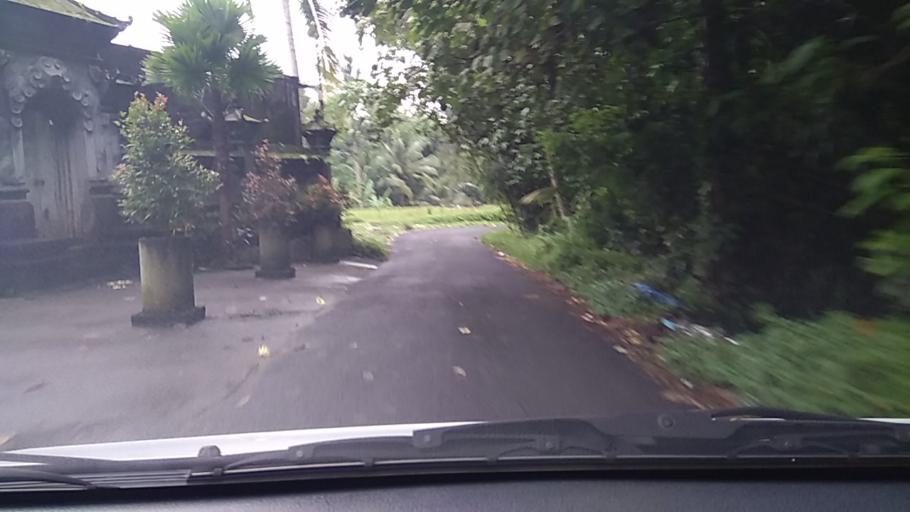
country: ID
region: Bali
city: Banjar Dujung Kaja
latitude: -8.4120
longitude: 115.2861
